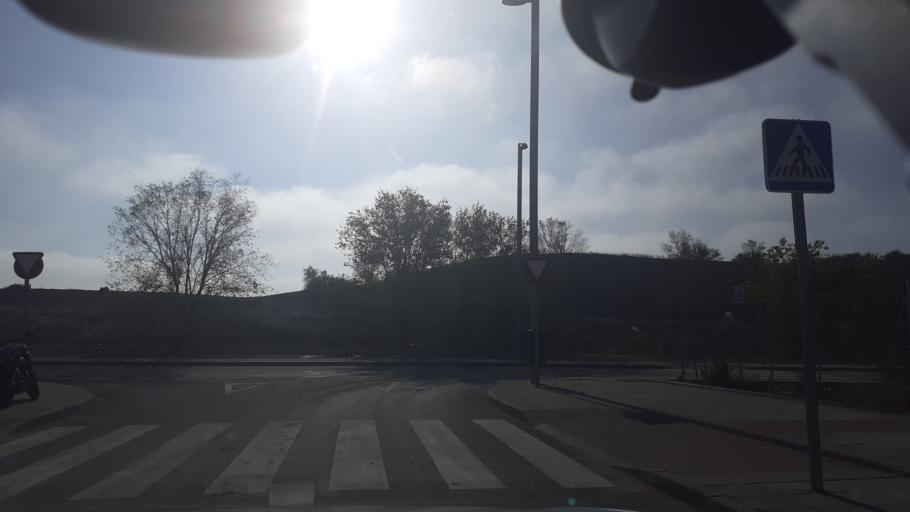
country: ES
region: Madrid
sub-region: Provincia de Madrid
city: Coslada
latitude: 40.3969
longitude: -3.5586
